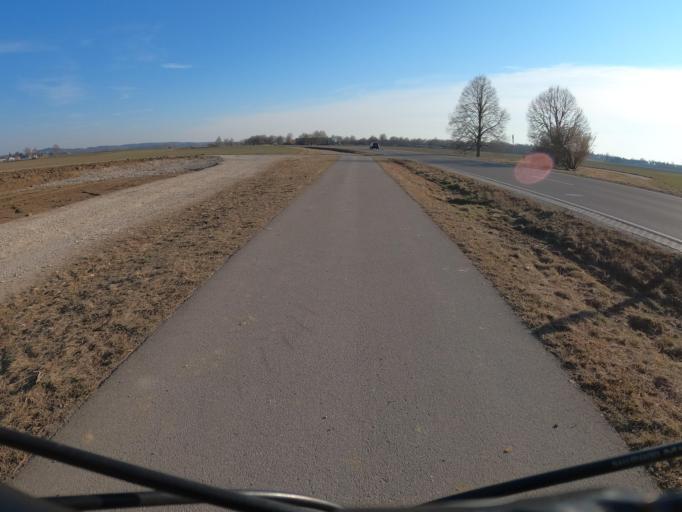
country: DE
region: Bavaria
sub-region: Swabia
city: Neu-Ulm
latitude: 48.4185
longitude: 10.0555
